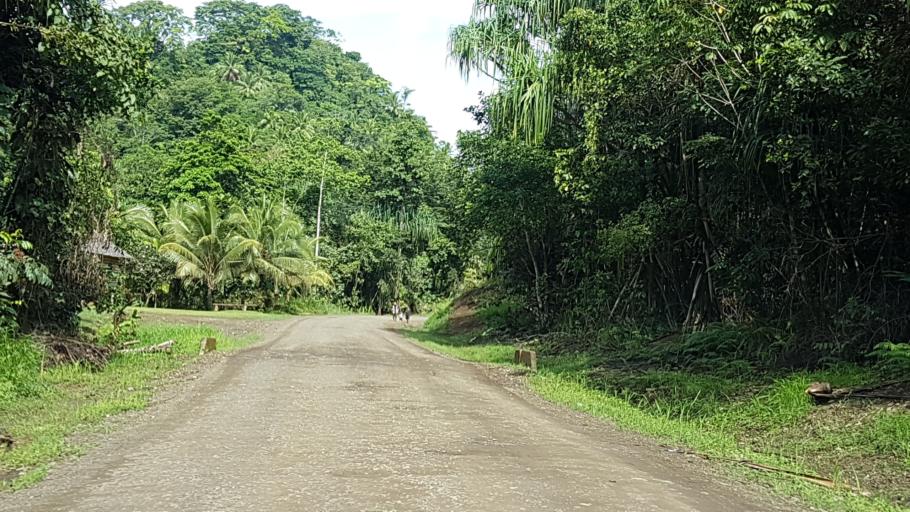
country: PG
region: Milne Bay
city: Alotau
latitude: -10.3386
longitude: 150.6115
